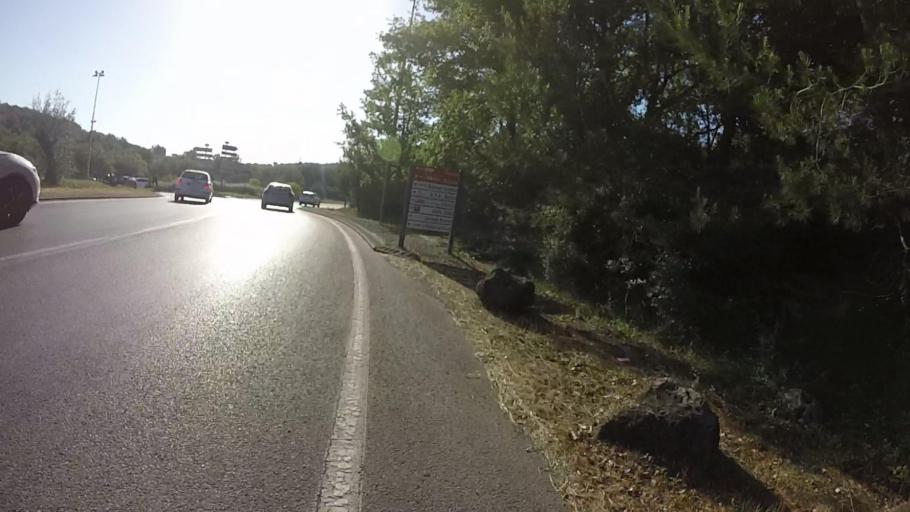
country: FR
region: Provence-Alpes-Cote d'Azur
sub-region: Departement des Alpes-Maritimes
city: Mougins
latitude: 43.6166
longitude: 7.0378
